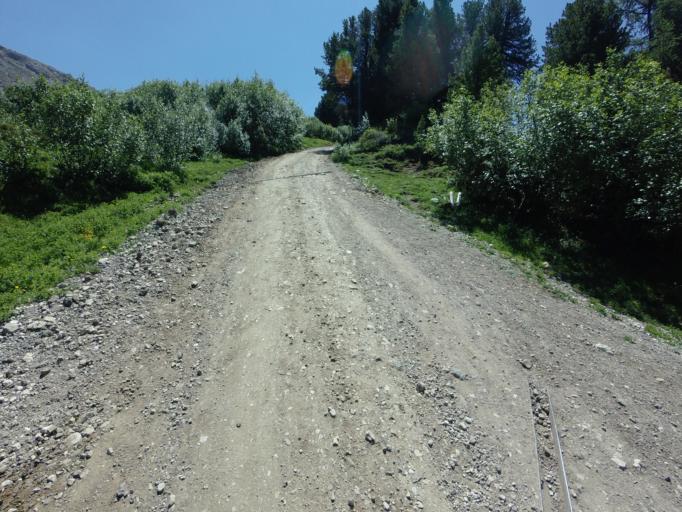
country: IT
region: Trentino-Alto Adige
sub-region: Provincia di Trento
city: Mazzin
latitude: 46.5110
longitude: 11.6920
